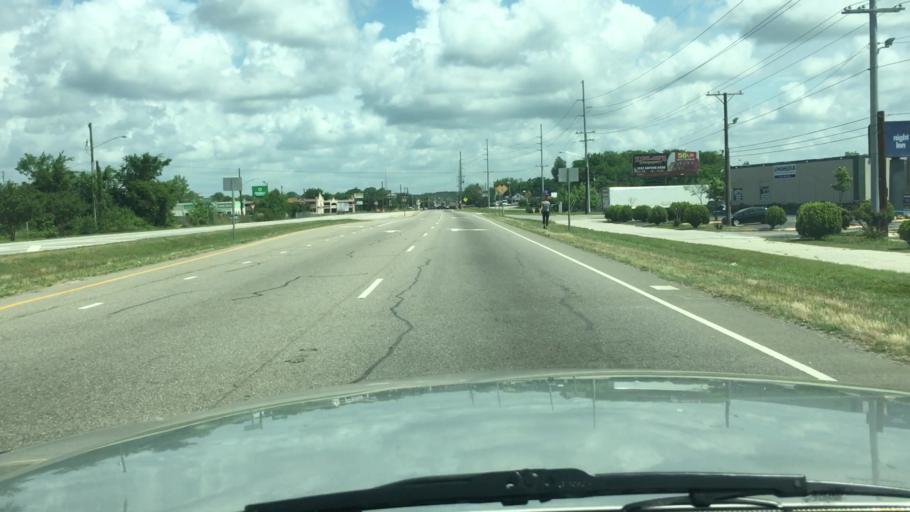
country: US
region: North Carolina
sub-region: Cumberland County
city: Fayetteville
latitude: 35.0411
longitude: -78.8662
